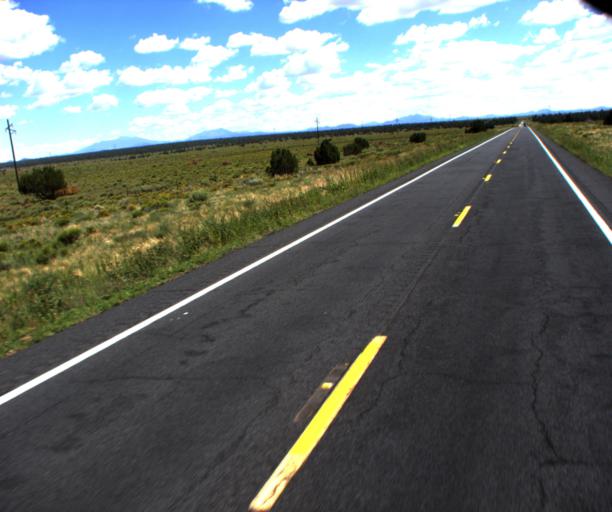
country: US
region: Arizona
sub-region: Coconino County
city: Grand Canyon Village
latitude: 35.7947
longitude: -112.1304
